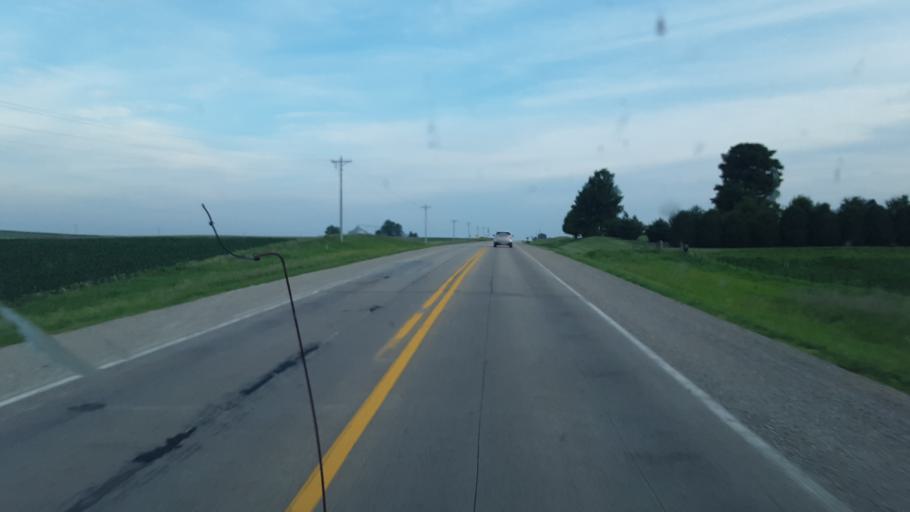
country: US
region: Iowa
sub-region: Benton County
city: Belle Plaine
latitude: 41.8037
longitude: -92.2788
